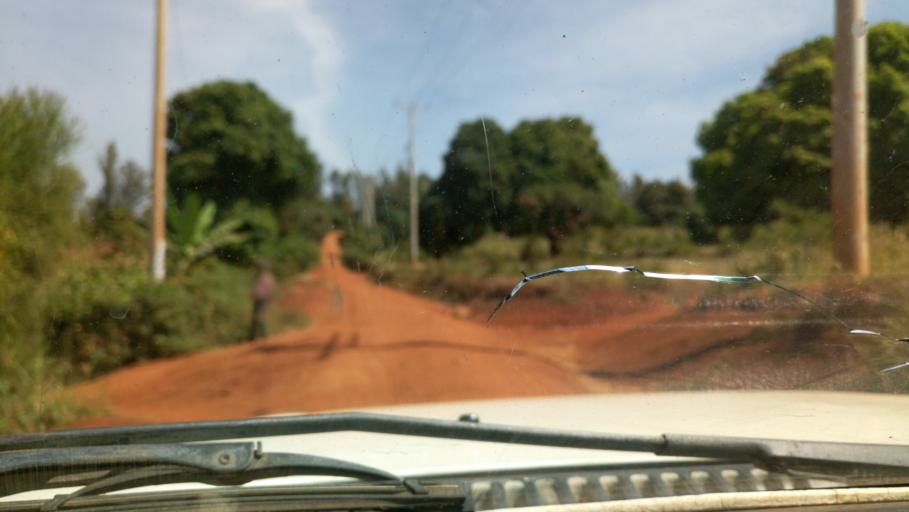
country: KE
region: Murang'a District
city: Murang'a
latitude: -0.7381
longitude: 37.1479
